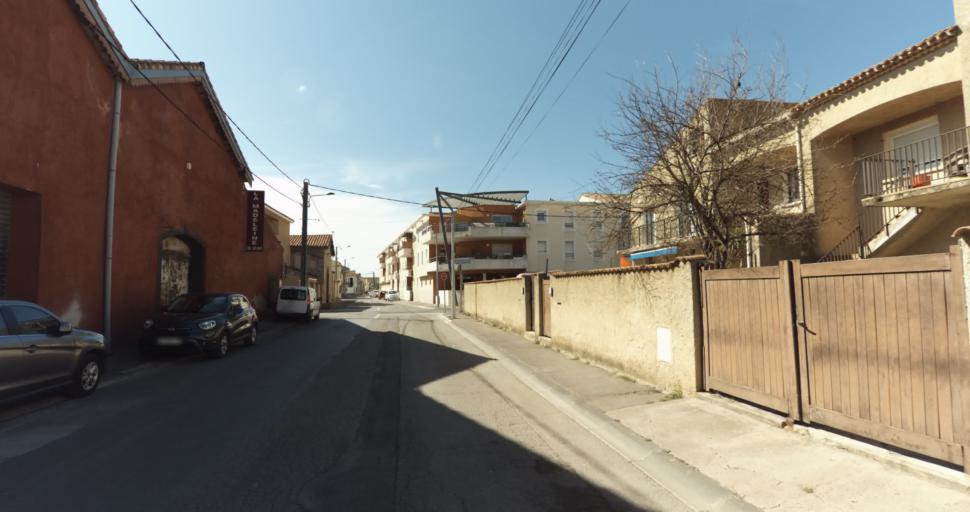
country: FR
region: Languedoc-Roussillon
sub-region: Departement de l'Herault
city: Marseillan
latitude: 43.3558
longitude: 3.5332
